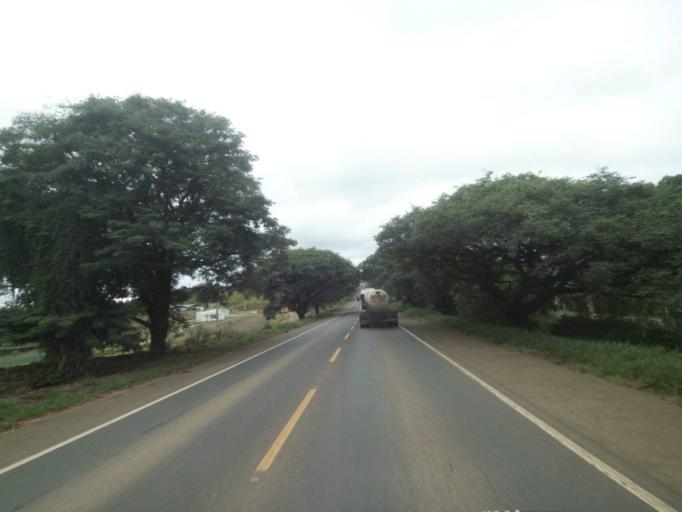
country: BR
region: Parana
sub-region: Telemaco Borba
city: Telemaco Borba
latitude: -24.3508
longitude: -50.6604
